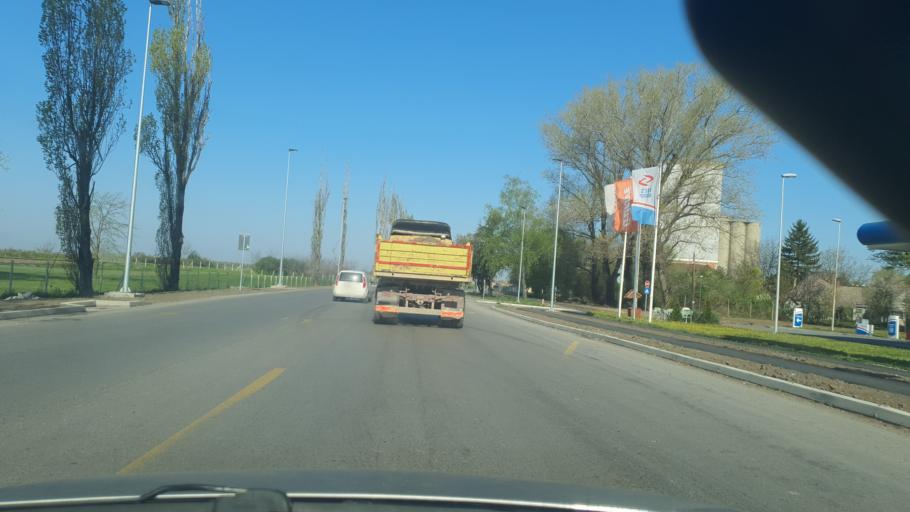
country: RS
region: Autonomna Pokrajina Vojvodina
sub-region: Juznobacki Okrug
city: Vrbas
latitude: 45.5825
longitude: 19.6176
